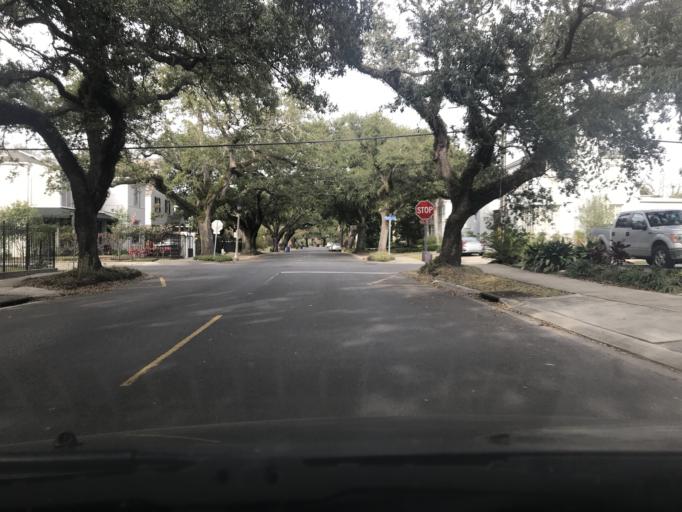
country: US
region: Louisiana
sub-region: Orleans Parish
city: New Orleans
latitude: 29.9525
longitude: -90.1082
